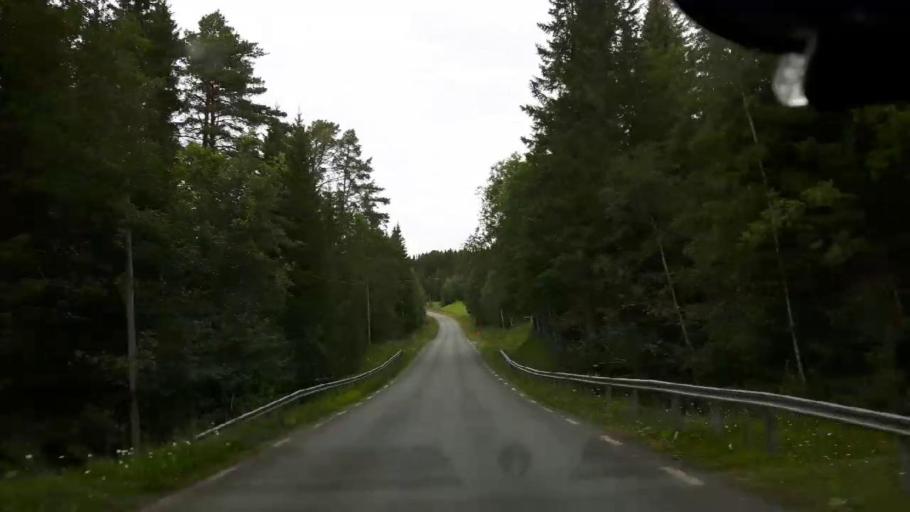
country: SE
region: Jaemtland
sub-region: Krokoms Kommun
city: Valla
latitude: 63.4788
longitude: 14.0613
